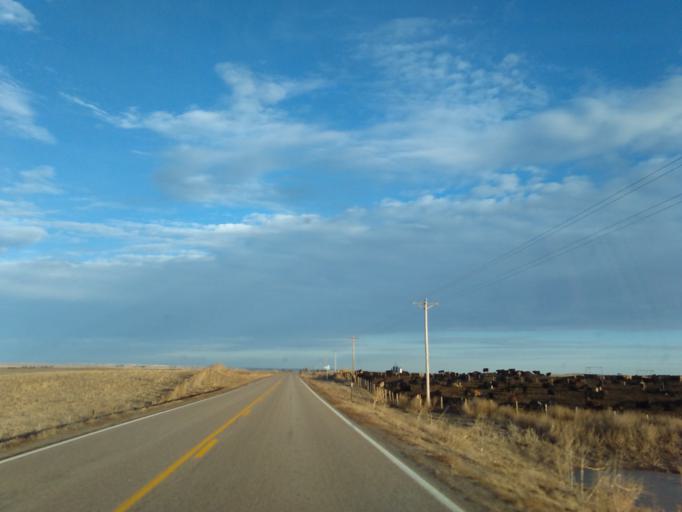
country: US
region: Nebraska
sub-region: Morrill County
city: Bridgeport
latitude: 41.5982
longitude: -102.9723
